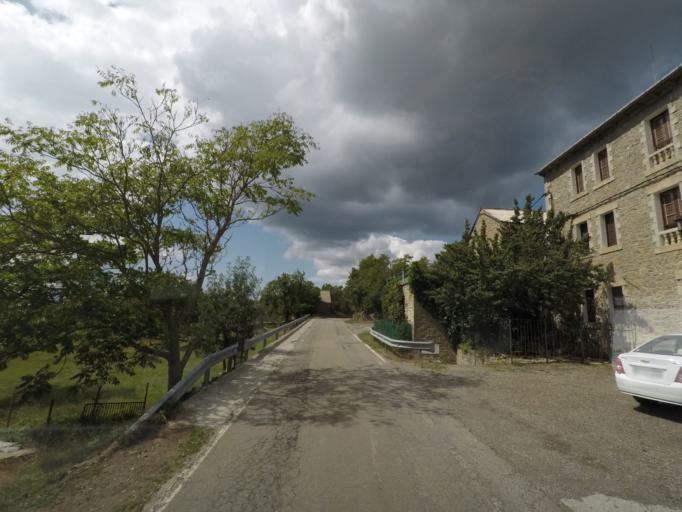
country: ES
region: Aragon
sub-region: Provincia de Huesca
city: Fiscal
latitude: 42.4136
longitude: -0.1188
